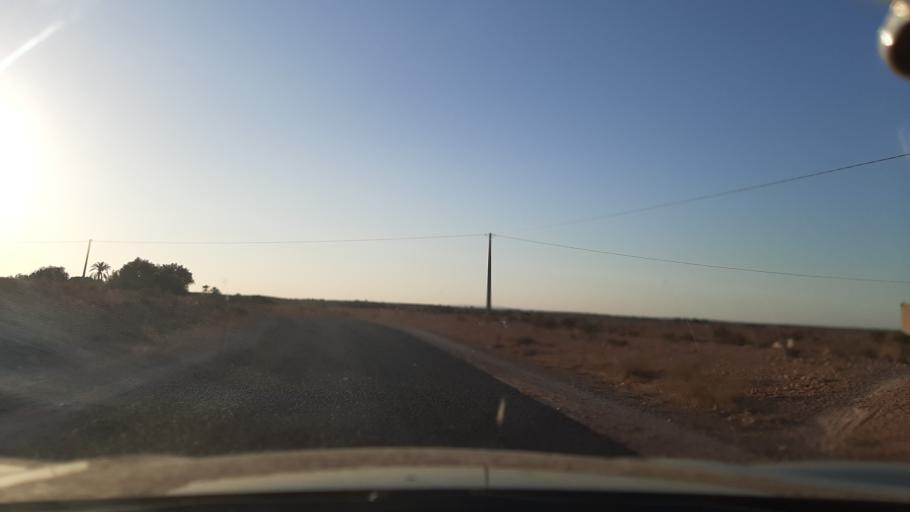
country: TN
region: Qabis
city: Matmata
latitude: 33.6228
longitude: 10.1391
